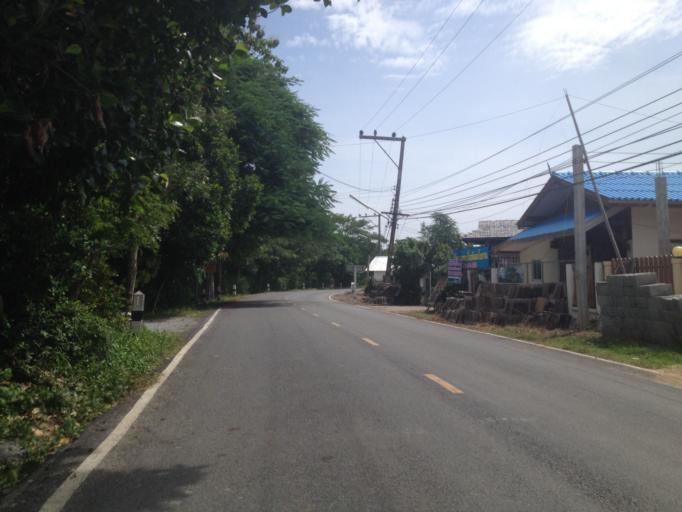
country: TH
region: Chiang Mai
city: Hang Dong
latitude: 18.6663
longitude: 98.9684
